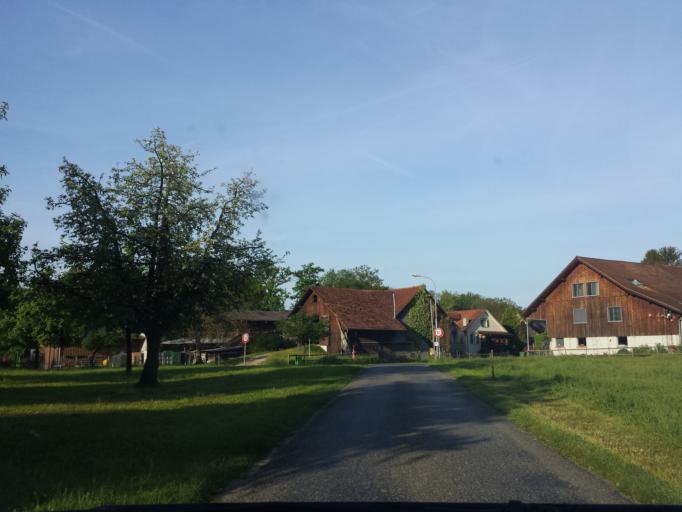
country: CH
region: Thurgau
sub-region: Arbon District
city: Egnach
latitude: 47.5427
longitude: 9.3679
